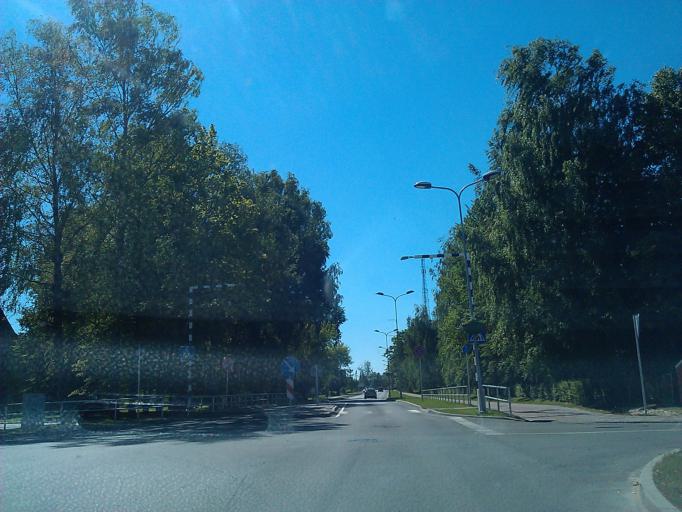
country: LV
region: Vilanu
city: Vilani
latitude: 56.5458
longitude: 26.9248
